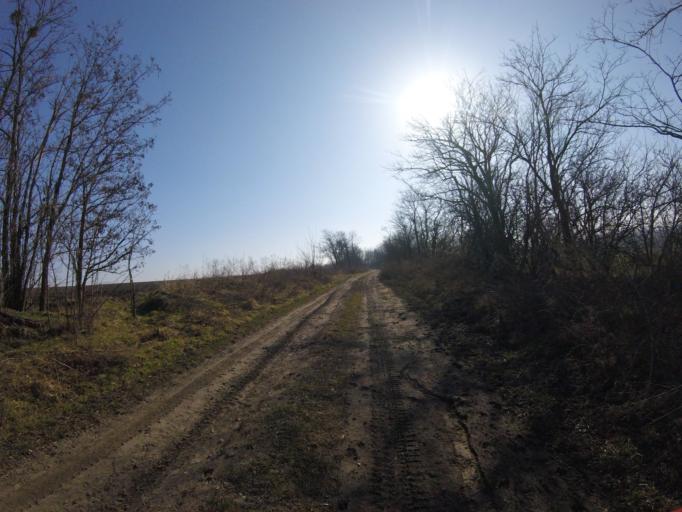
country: HU
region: Komarom-Esztergom
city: Bokod
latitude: 47.5296
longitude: 18.1984
